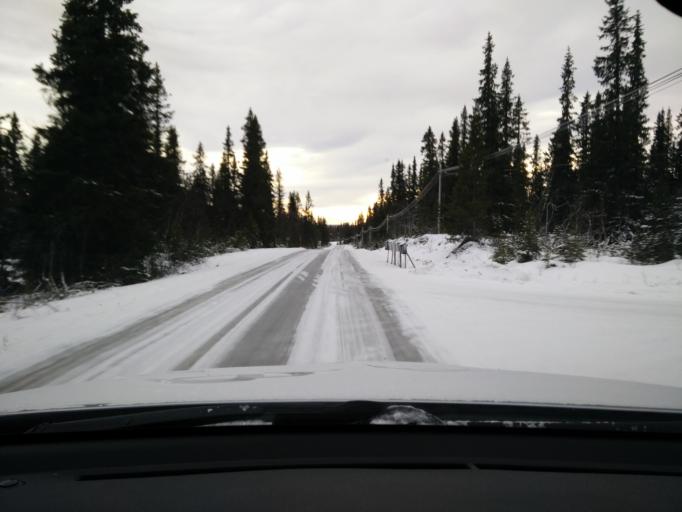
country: SE
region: Jaemtland
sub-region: Bergs Kommun
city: Hoverberg
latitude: 62.4854
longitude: 14.1202
